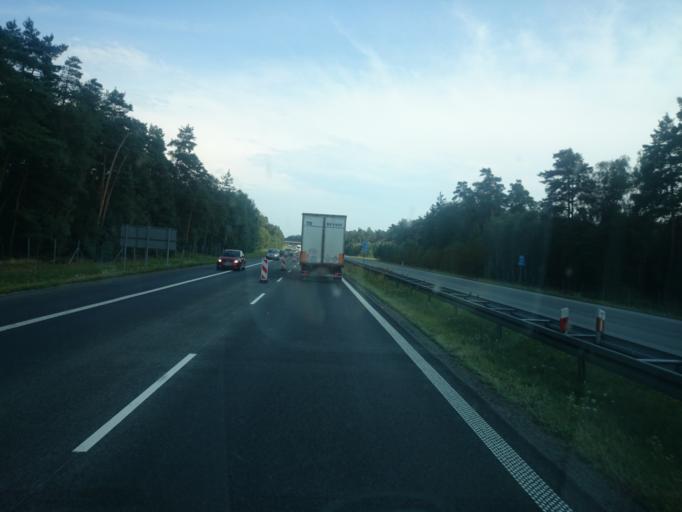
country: PL
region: Opole Voivodeship
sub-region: Powiat opolski
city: Dabrowa
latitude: 50.6381
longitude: 17.7368
